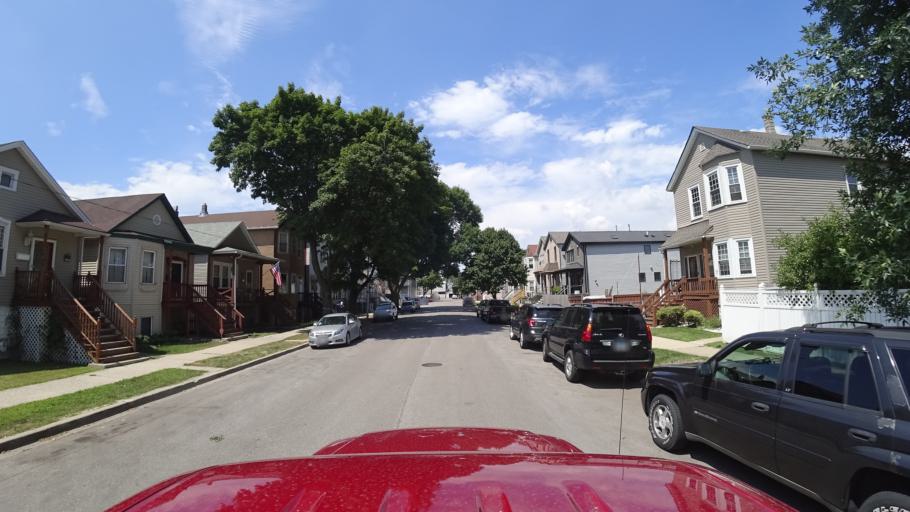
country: US
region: Illinois
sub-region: Cook County
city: Chicago
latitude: 41.8099
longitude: -87.6414
